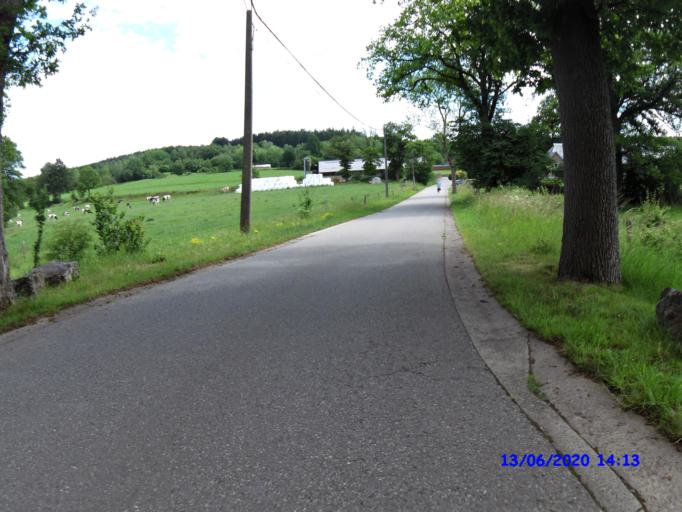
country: BE
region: Wallonia
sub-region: Province de Liege
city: Stavelot
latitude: 50.4121
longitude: 5.9693
